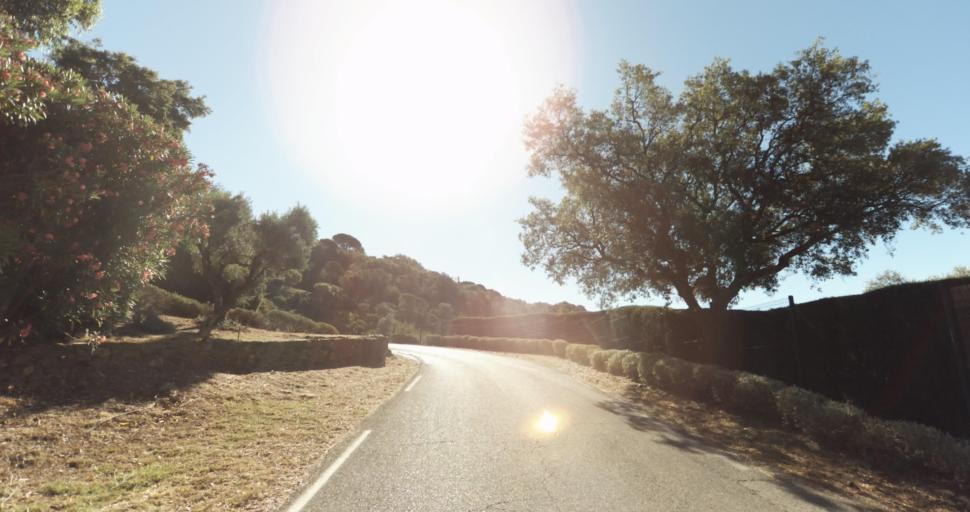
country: FR
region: Provence-Alpes-Cote d'Azur
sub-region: Departement du Var
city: Ramatuelle
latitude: 43.2175
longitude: 6.5982
